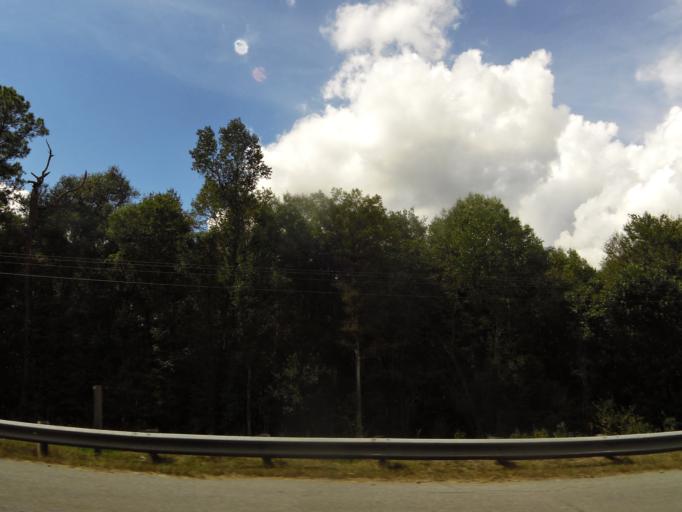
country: US
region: Georgia
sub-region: Brantley County
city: Nahunta
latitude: 31.0972
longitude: -82.0061
